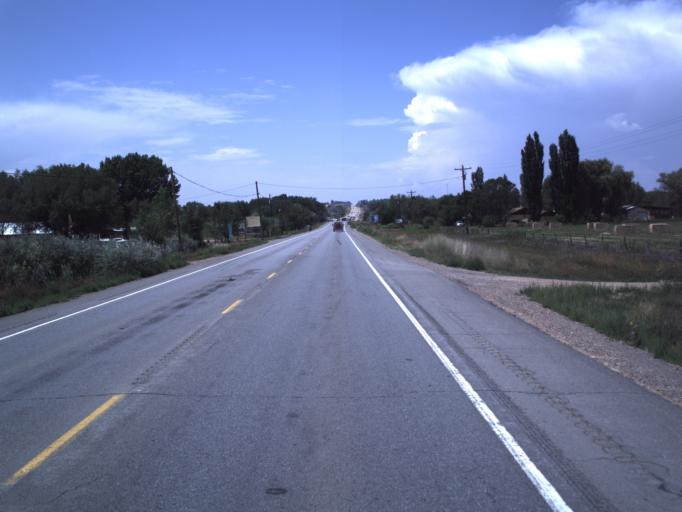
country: US
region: Utah
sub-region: Duchesne County
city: Roosevelt
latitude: 40.3019
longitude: -109.8469
